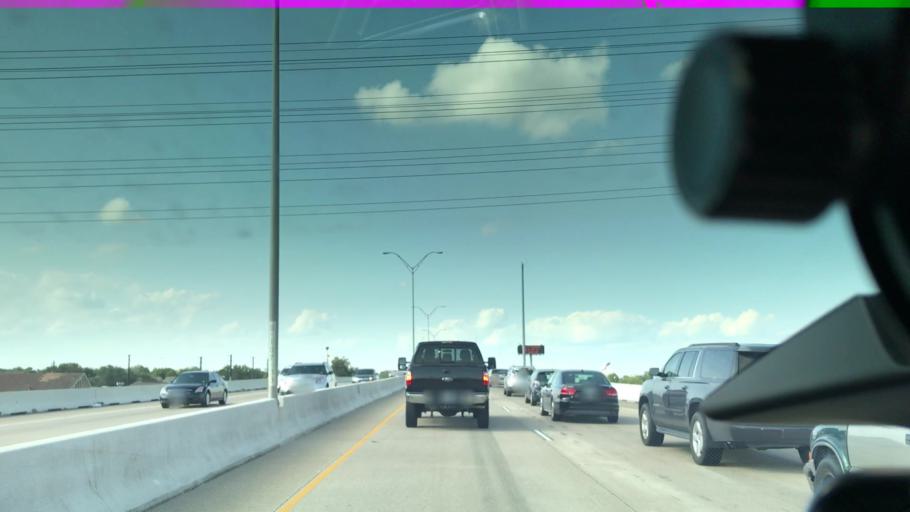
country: US
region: Texas
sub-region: Harris County
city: Deer Park
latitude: 29.6996
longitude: -95.1534
